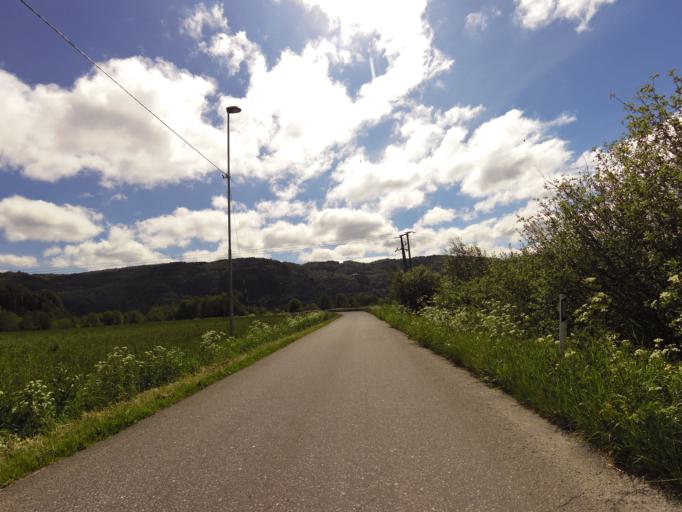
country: NO
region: Vest-Agder
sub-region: Kvinesdal
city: Liknes
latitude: 58.3071
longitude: 6.9362
